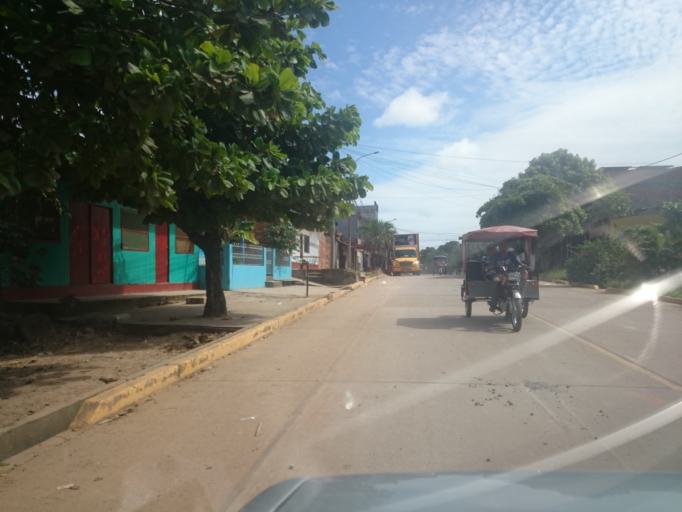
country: PE
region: Ucayali
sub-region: Provincia de Coronel Portillo
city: Puerto Callao
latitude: -8.3554
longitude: -74.5772
